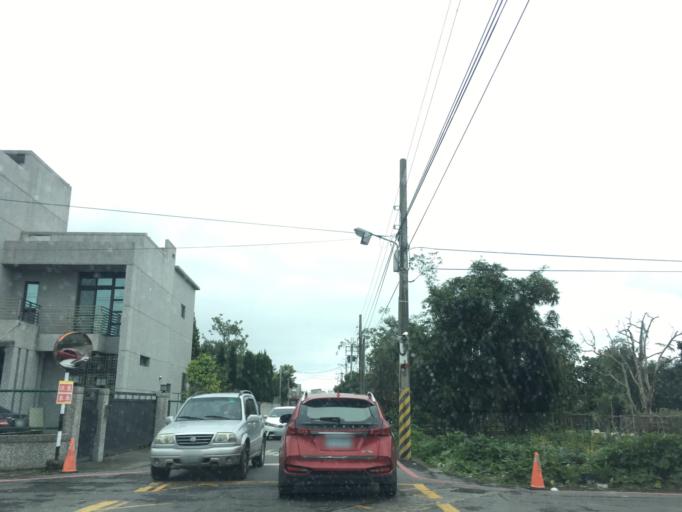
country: TW
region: Taiwan
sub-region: Hualien
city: Hualian
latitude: 23.9914
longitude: 121.5717
